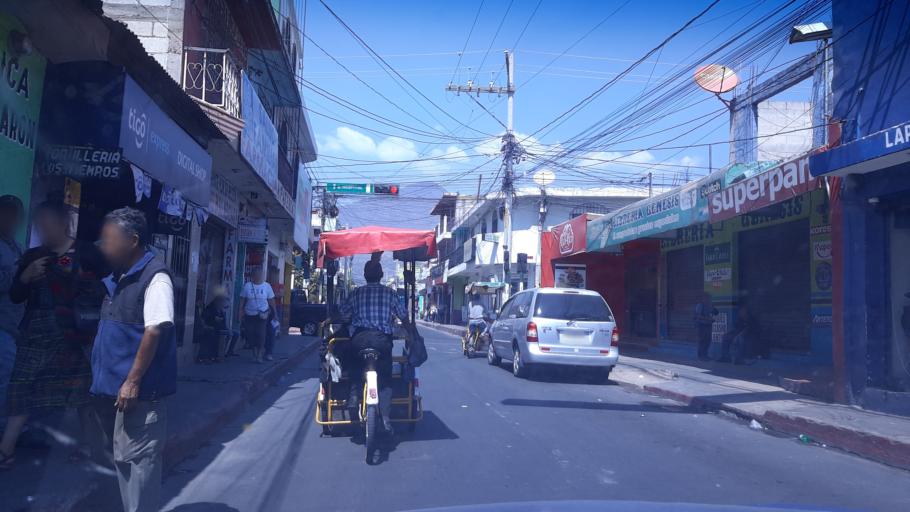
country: GT
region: Guatemala
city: Amatitlan
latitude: 14.4799
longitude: -90.6203
